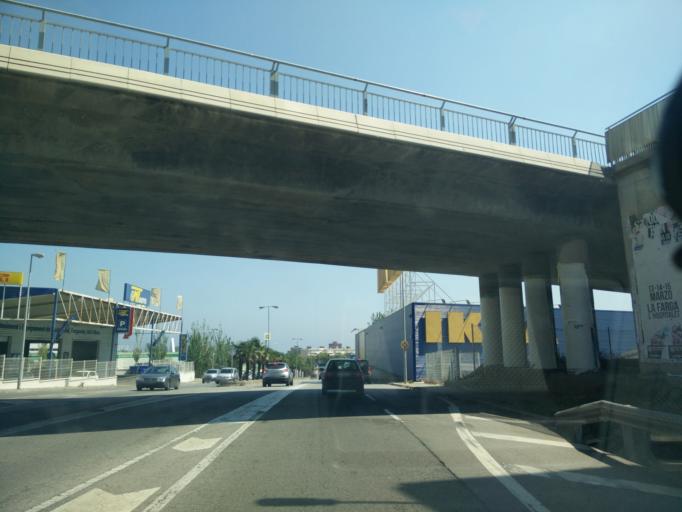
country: ES
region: Catalonia
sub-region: Provincia de Barcelona
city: Santa Coloma de Gramenet
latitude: 41.4606
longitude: 2.2255
